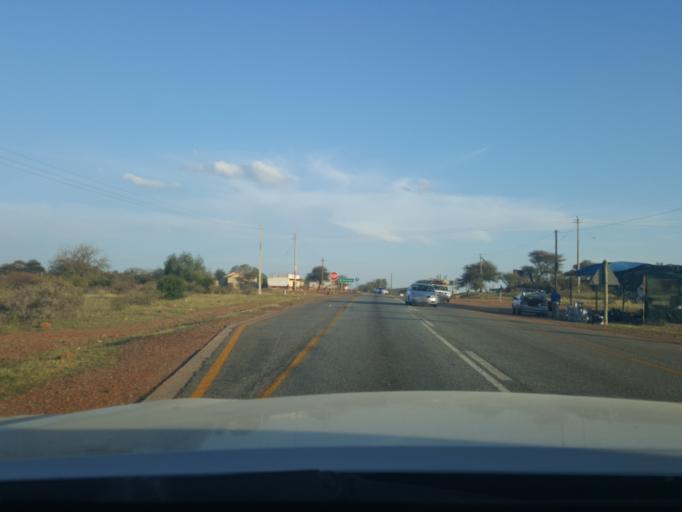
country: ZA
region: North-West
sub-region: Ngaka Modiri Molema District Municipality
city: Zeerust
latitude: -25.3851
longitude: 26.0841
